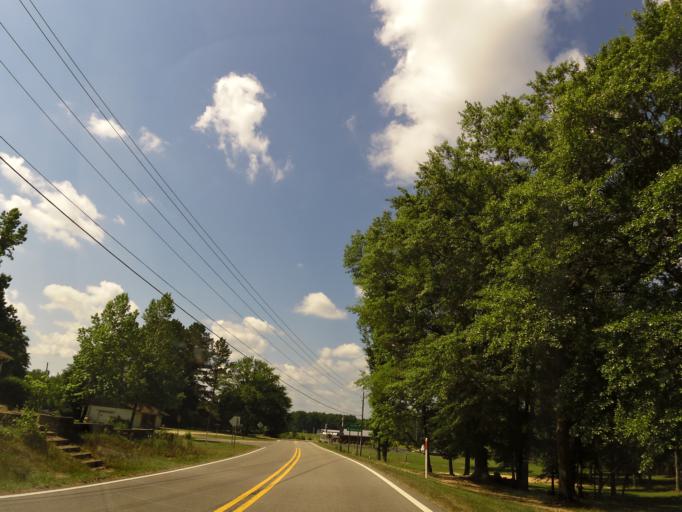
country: US
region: Alabama
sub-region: Marion County
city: Guin
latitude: 34.0048
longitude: -87.8572
